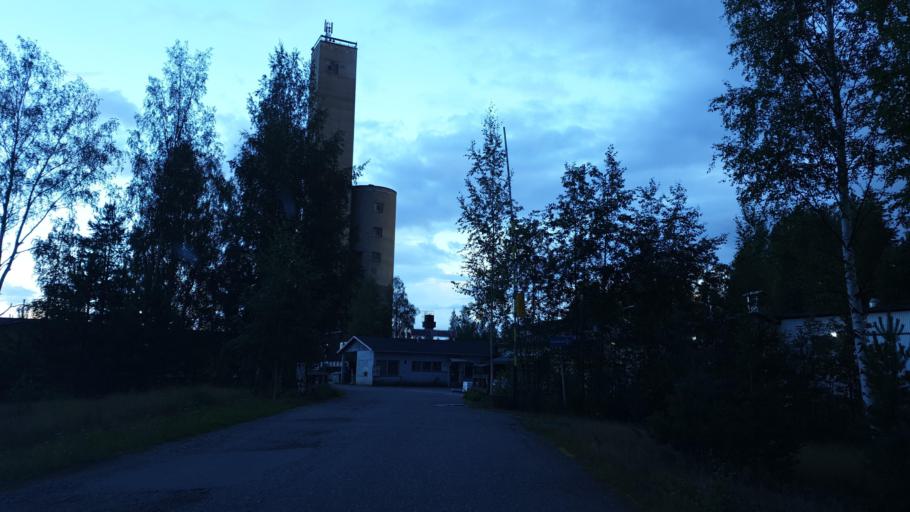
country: FI
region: Northern Savo
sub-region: Varkaus
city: Leppaevirta
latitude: 62.5816
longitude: 27.6069
